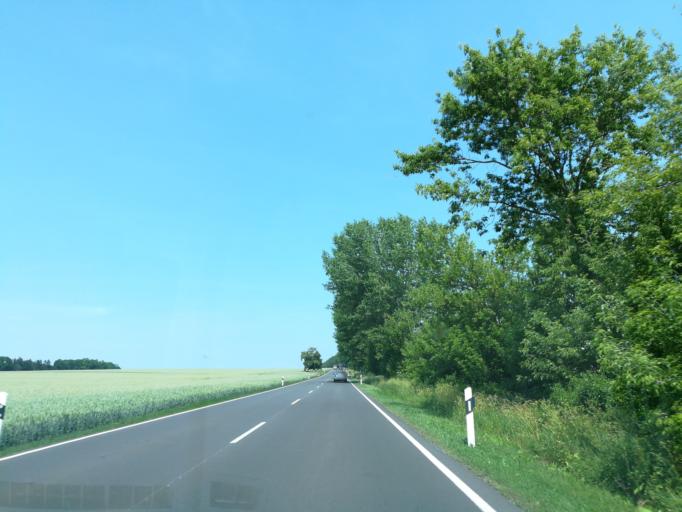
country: DE
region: Saxony-Anhalt
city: Gross Bornecke
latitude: 51.8295
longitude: 11.4566
